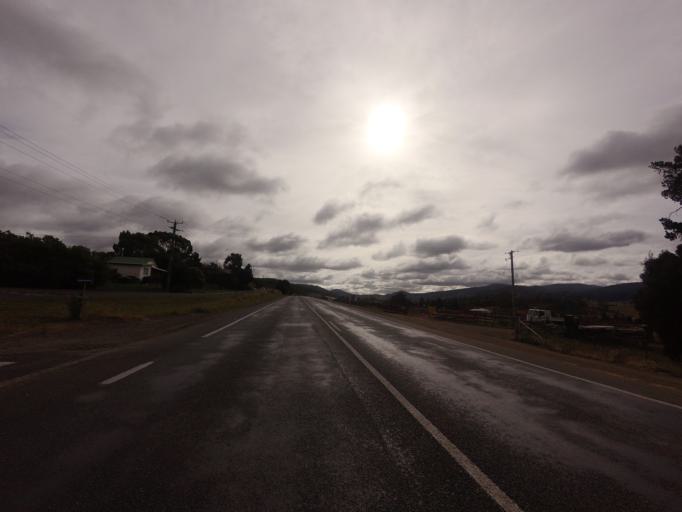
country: AU
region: Tasmania
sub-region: Brighton
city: Bridgewater
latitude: -42.6354
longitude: 147.2258
